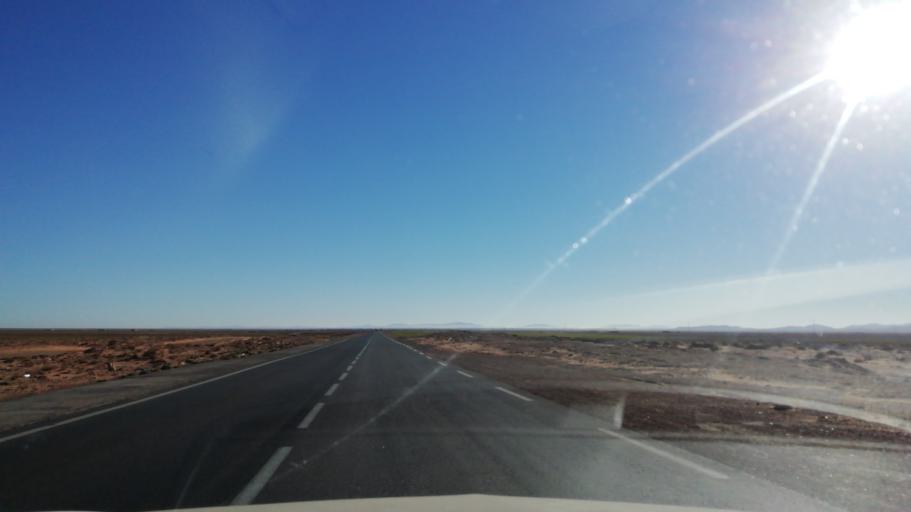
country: DZ
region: El Bayadh
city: El Bayadh
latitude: 33.8599
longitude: 0.5588
